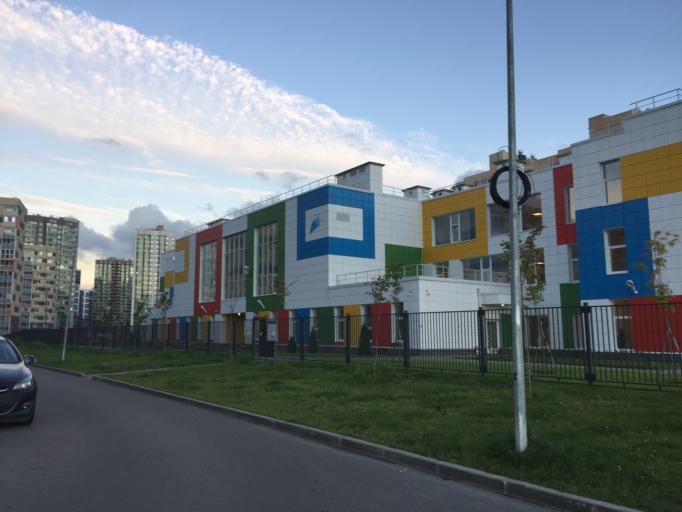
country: RU
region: St.-Petersburg
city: Grazhdanka
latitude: 60.0543
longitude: 30.4142
